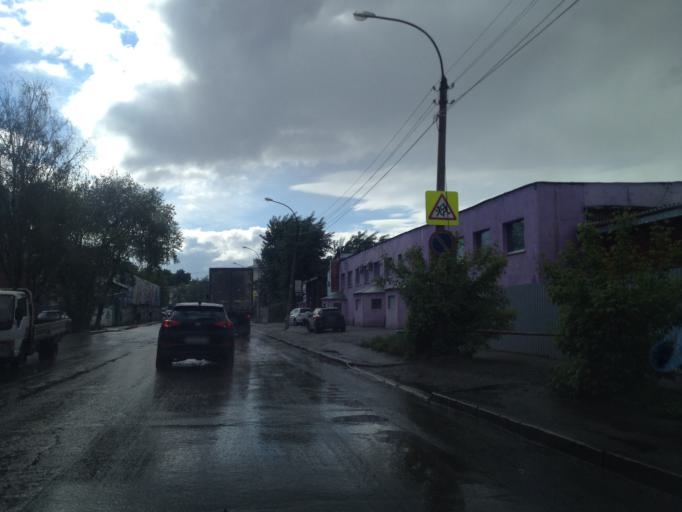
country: RU
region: Sverdlovsk
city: Yekaterinburg
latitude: 56.8668
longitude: 60.5858
